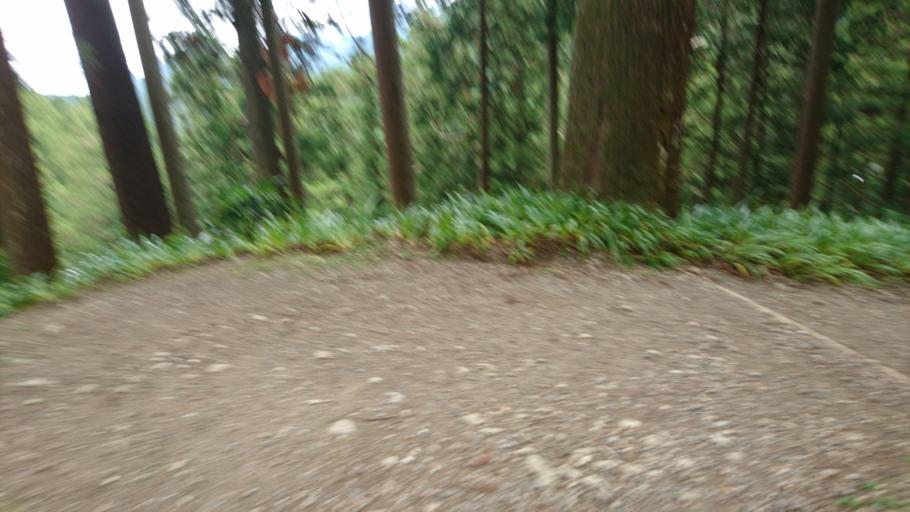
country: JP
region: Shizuoka
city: Fujinomiya
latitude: 35.3810
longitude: 138.4242
